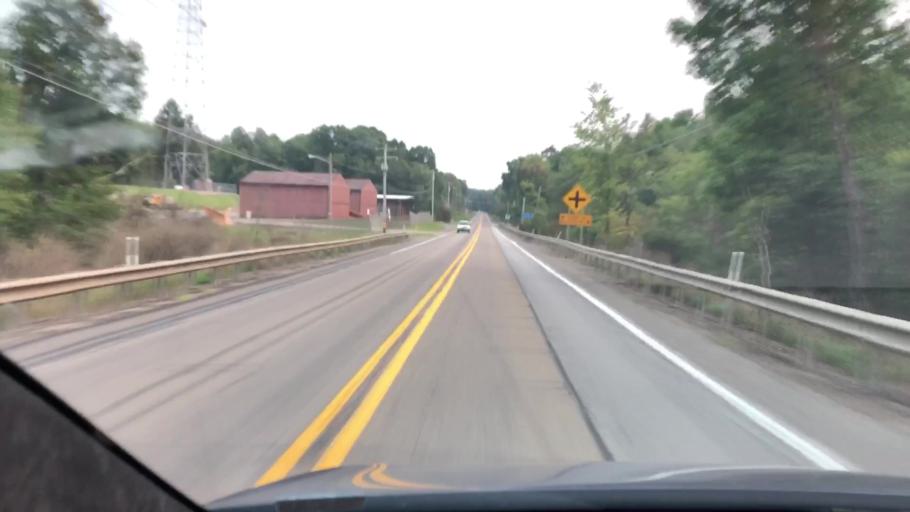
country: US
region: Pennsylvania
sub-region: Butler County
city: Slippery Rock
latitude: 41.0365
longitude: -80.0072
